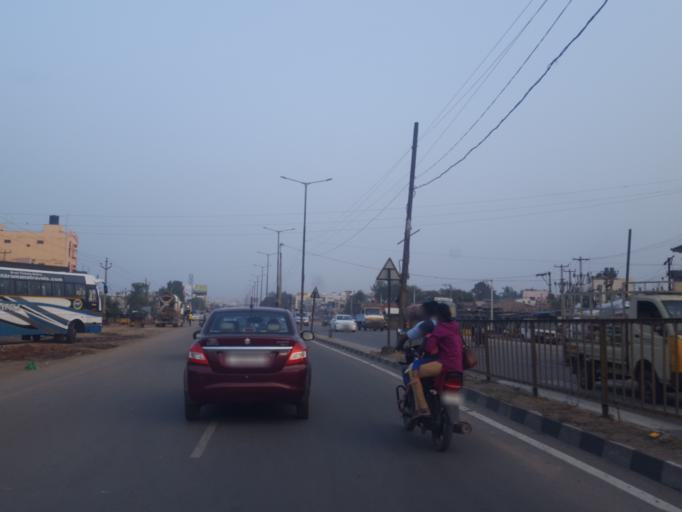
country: IN
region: Telangana
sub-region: Medak
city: Patancheru
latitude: 17.5148
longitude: 78.2845
